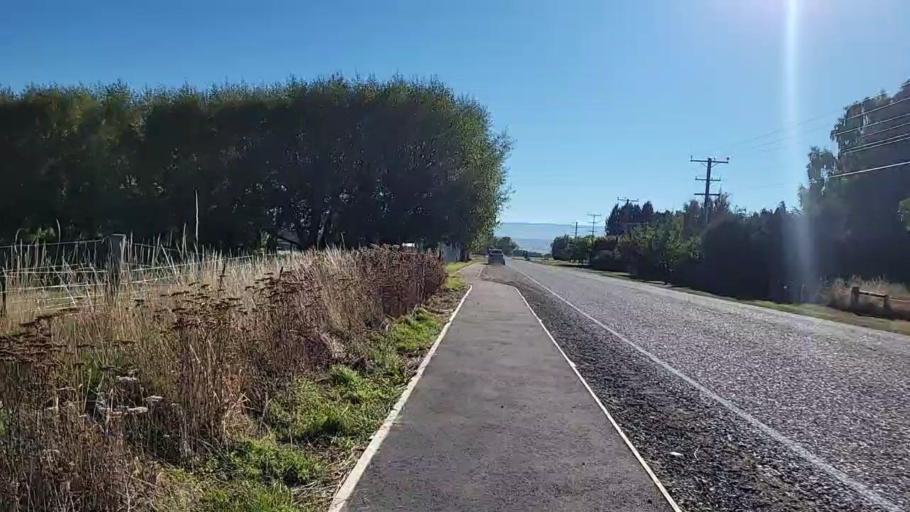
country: NZ
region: Otago
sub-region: Queenstown-Lakes District
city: Wanaka
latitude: -45.0035
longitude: 169.9163
